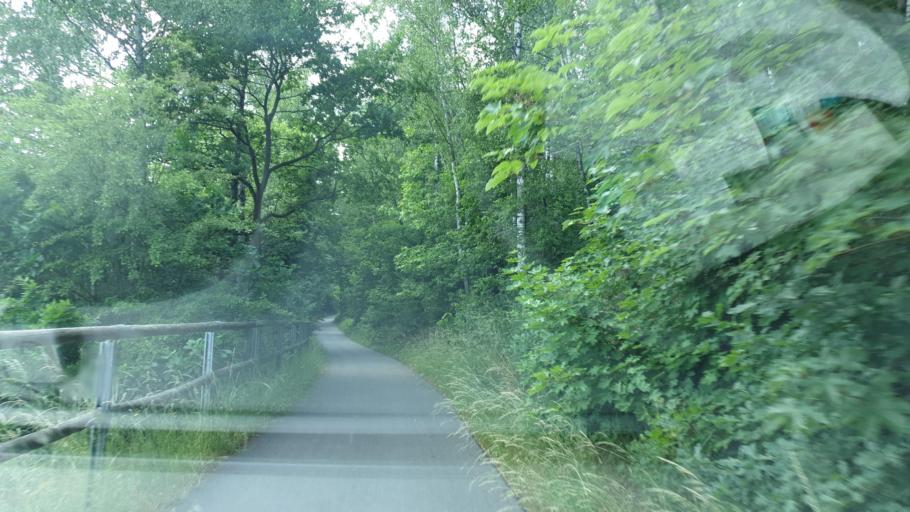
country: DE
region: Saxony
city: Adorf
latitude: 50.3442
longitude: 12.2460
